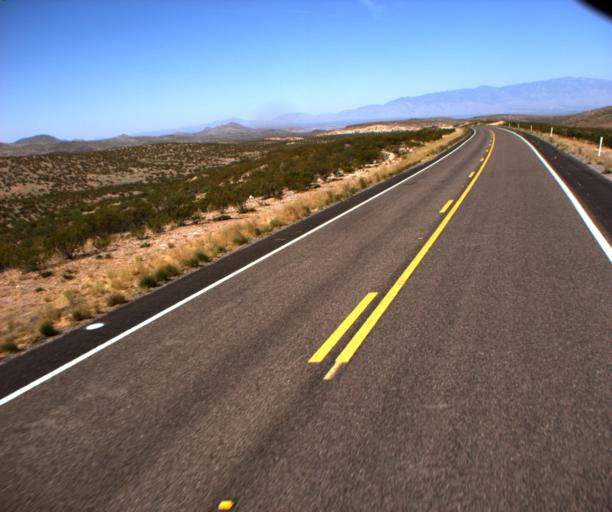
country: US
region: Arizona
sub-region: Greenlee County
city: Clifton
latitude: 32.7538
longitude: -109.3708
